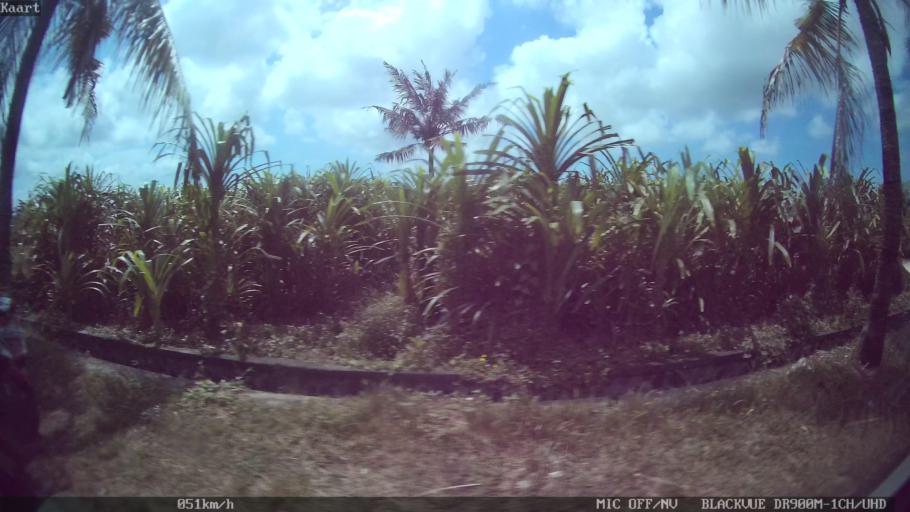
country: ID
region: Bali
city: Banjar Desa
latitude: -8.5798
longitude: 115.2877
